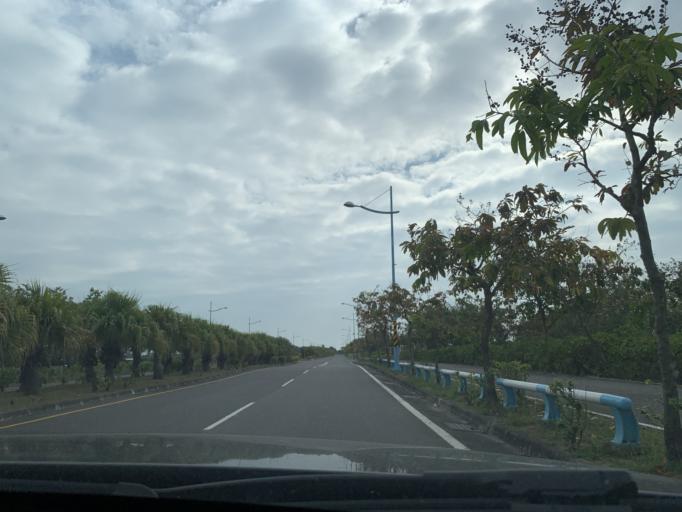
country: TW
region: Taiwan
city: Fengshan
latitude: 22.4496
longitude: 120.4877
